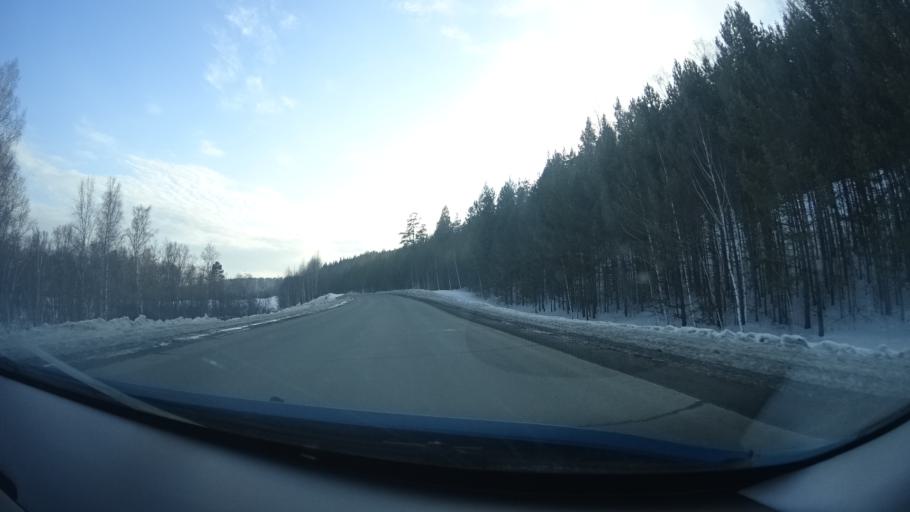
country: RU
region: Bashkortostan
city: Abzakovo
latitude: 53.4533
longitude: 58.3146
